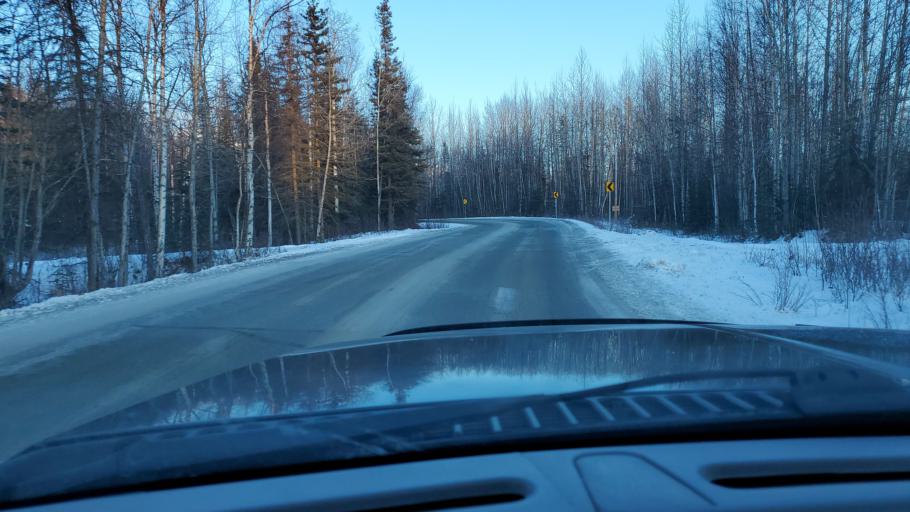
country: US
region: Alaska
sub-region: Matanuska-Susitna Borough
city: Fishhook
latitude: 61.6872
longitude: -149.2458
